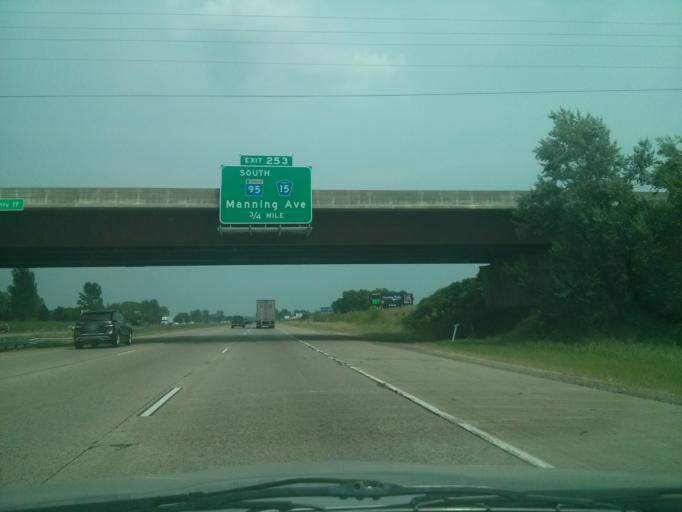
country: US
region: Minnesota
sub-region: Washington County
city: Lake Elmo
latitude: 44.9485
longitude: -92.8838
